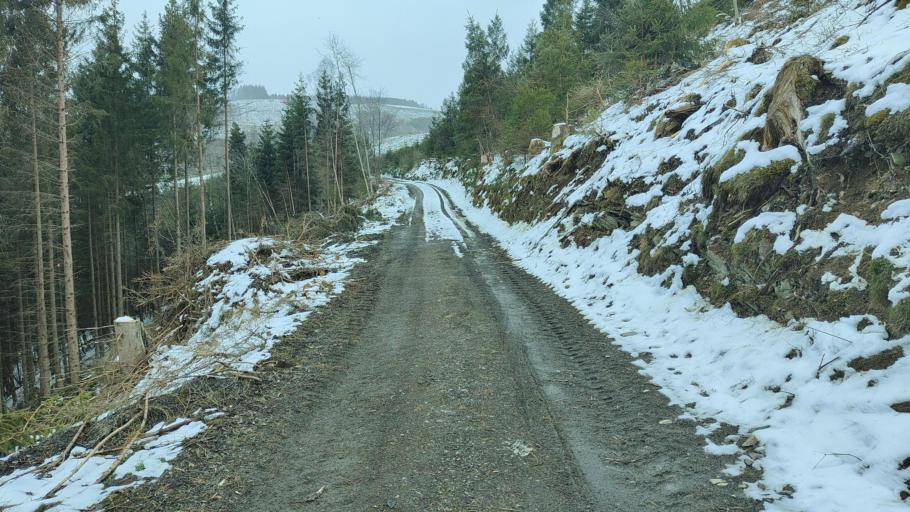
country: DE
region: North Rhine-Westphalia
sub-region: Regierungsbezirk Arnsberg
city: Bad Berleburg
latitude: 51.0835
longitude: 8.4260
